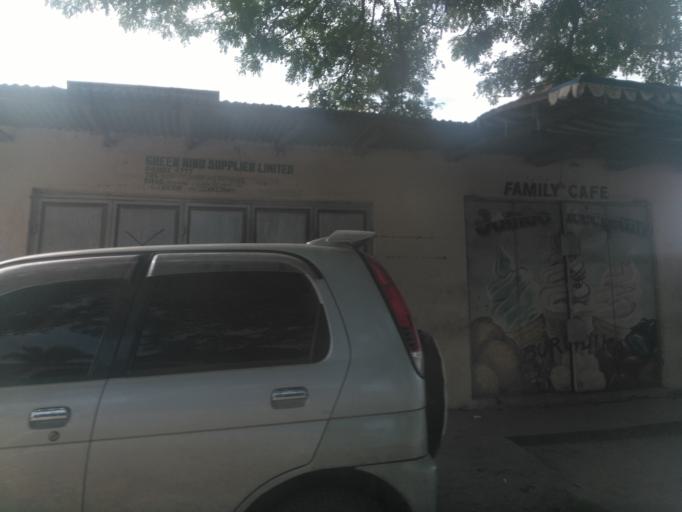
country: TZ
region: Zanzibar Urban/West
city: Zanzibar
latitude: -6.1586
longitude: 39.2056
